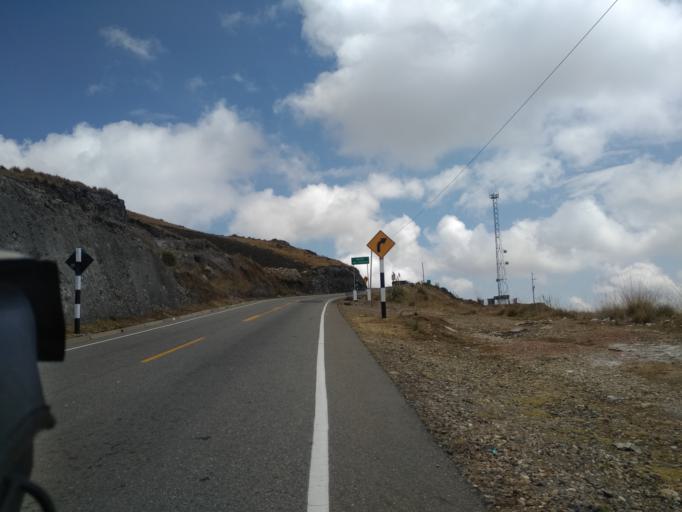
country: PE
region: La Libertad
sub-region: Provincia de Santiago de Chuco
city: Quiruvilca
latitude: -7.9183
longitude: -78.1585
